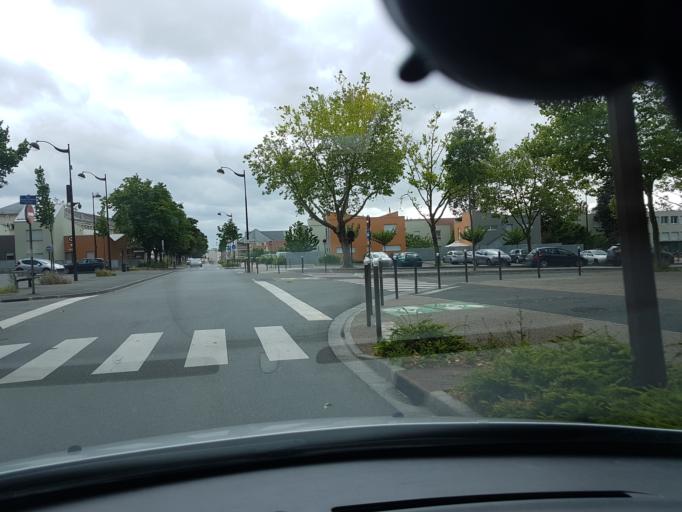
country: FR
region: Centre
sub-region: Departement du Cher
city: Bourges
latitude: 47.1100
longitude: 2.4109
